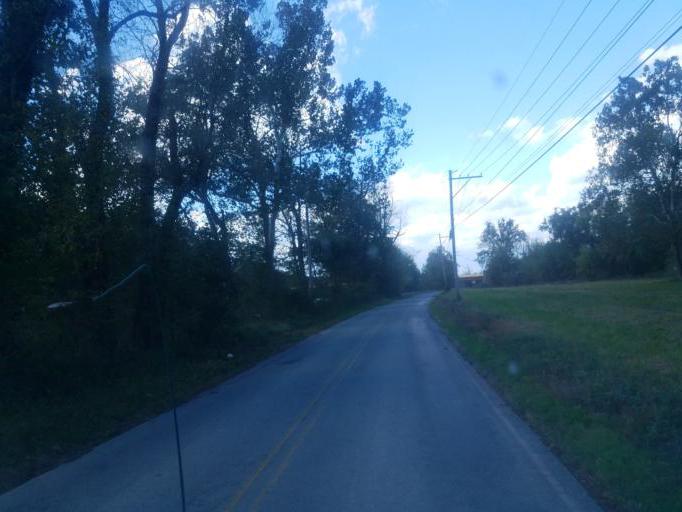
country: US
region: Pennsylvania
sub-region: Dauphin County
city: Middletown
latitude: 40.2073
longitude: -76.7145
